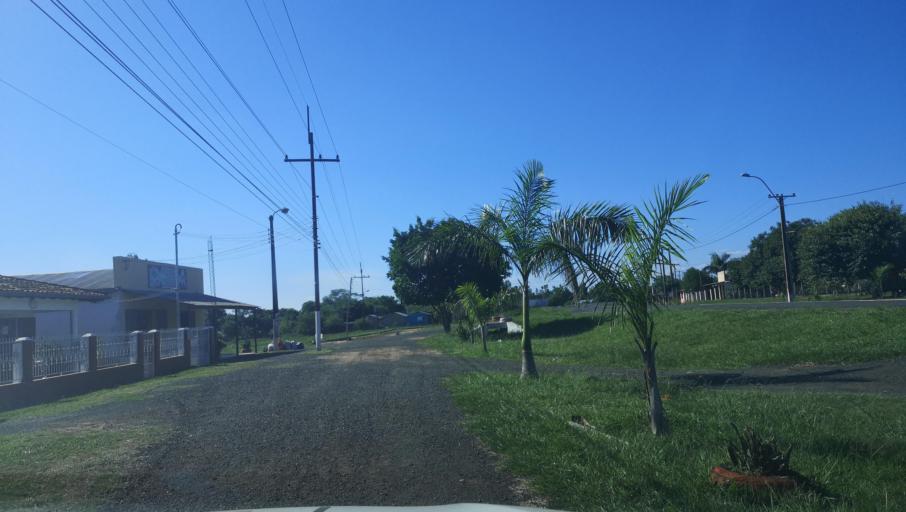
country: PY
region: Caaguazu
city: Carayao
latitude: -25.2043
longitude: -56.3993
